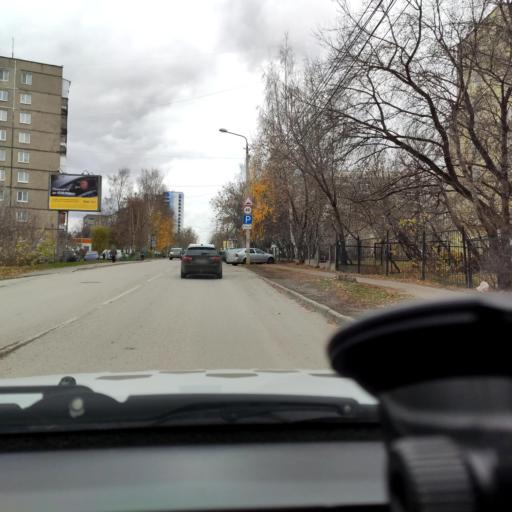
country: RU
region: Perm
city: Perm
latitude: 58.0288
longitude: 56.3101
